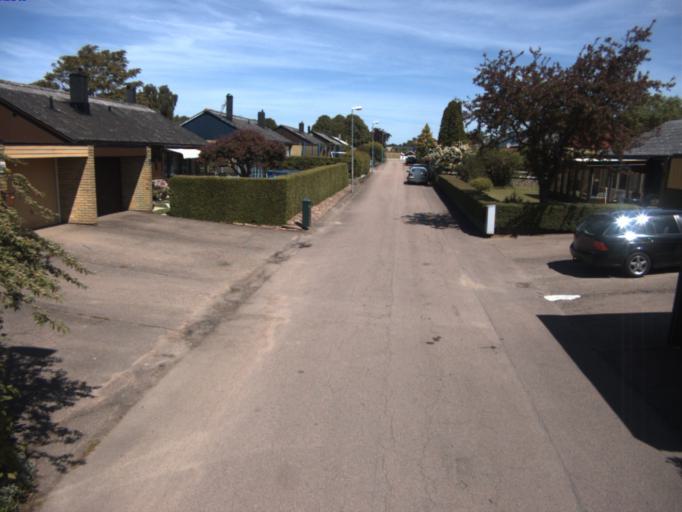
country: SE
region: Skane
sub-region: Helsingborg
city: Rydeback
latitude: 55.9667
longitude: 12.7691
